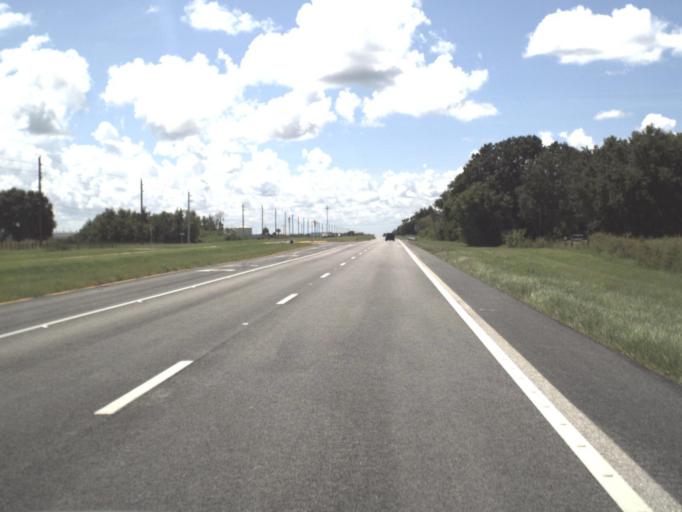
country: US
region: Florida
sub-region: Charlotte County
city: Harbour Heights
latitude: 27.0528
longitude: -81.9585
